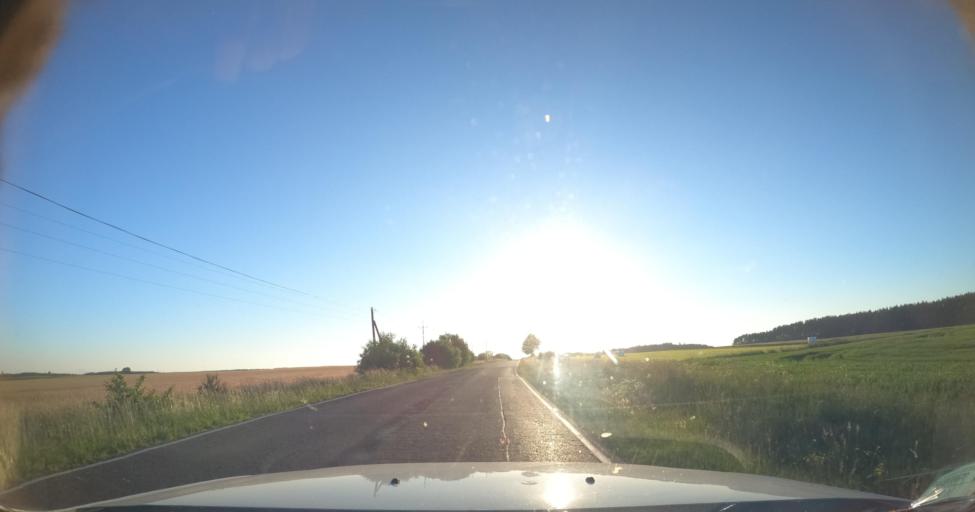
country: PL
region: Pomeranian Voivodeship
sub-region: Powiat bytowski
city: Czarna Dabrowka
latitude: 54.3623
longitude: 17.5232
